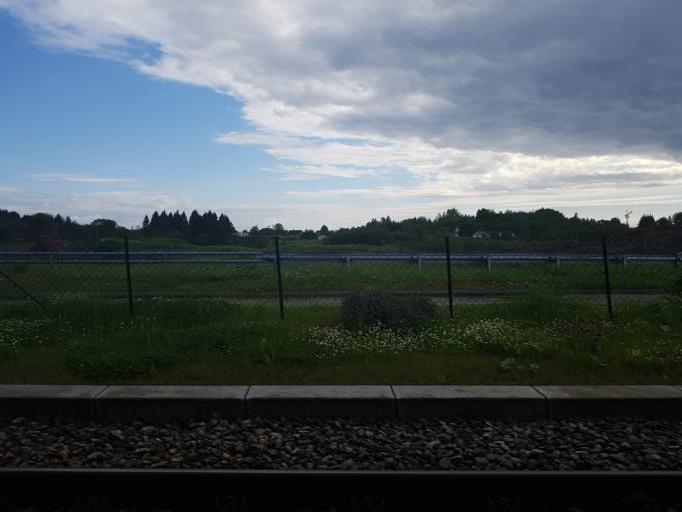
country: NO
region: Hordaland
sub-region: Bergen
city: Ytrebygda
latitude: 60.2916
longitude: 5.2474
